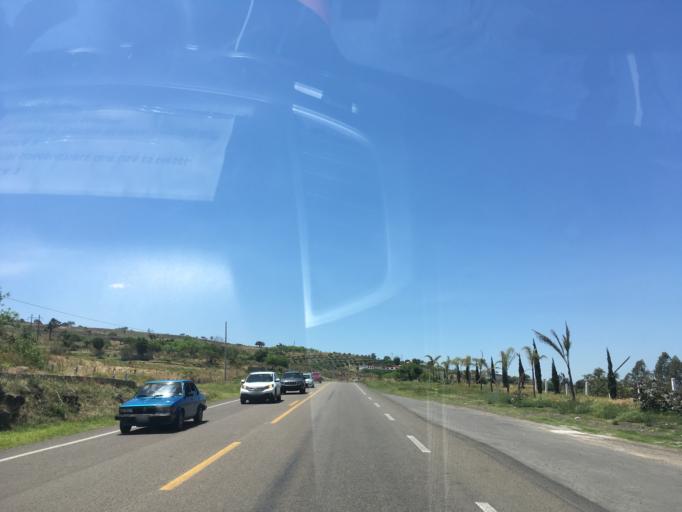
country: MX
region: Michoacan
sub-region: Tuxpan
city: La Soledad
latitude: 19.5282
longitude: -100.4738
